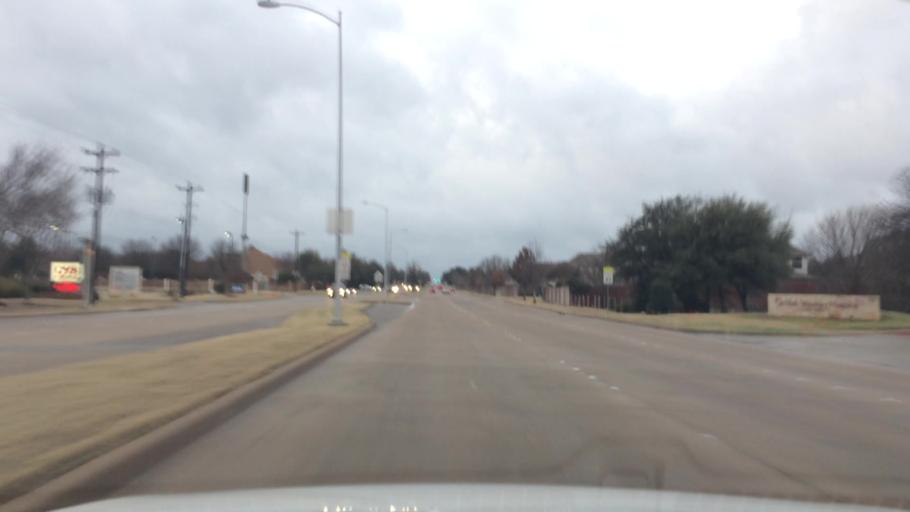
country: US
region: Texas
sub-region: Collin County
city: Frisco
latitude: 33.1007
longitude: -96.7716
